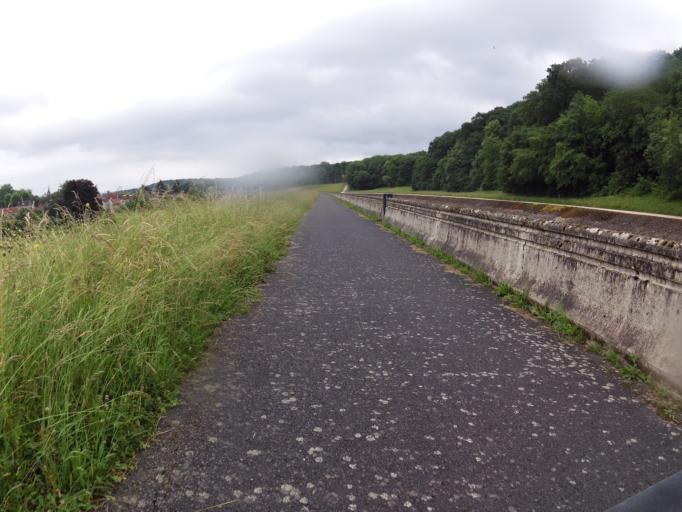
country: FR
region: Champagne-Ardenne
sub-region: Departement de la Haute-Marne
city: Saint-Dizier
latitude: 48.6155
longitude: 4.9007
